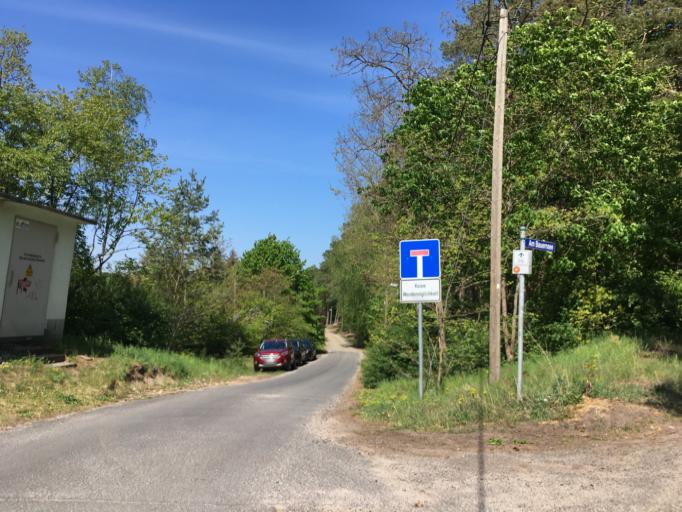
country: DE
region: Brandenburg
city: Marienwerder
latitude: 52.7897
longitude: 13.5562
